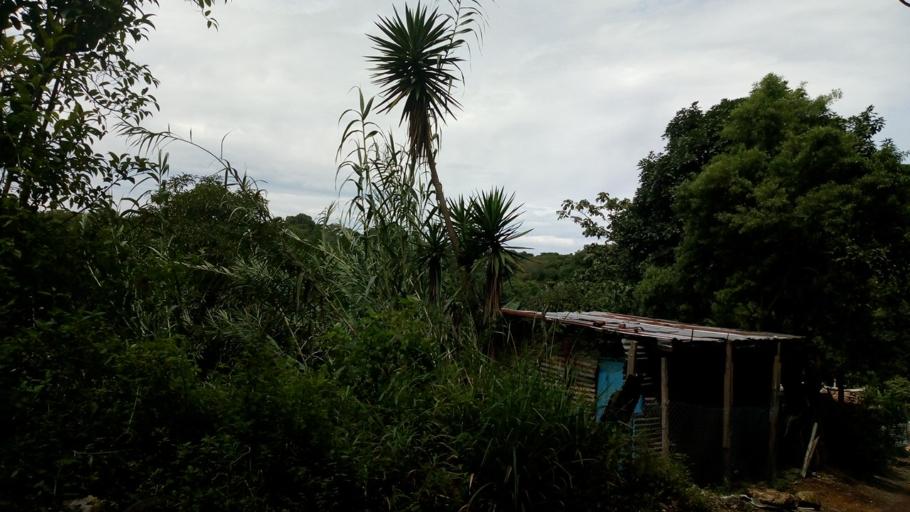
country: GT
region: Guatemala
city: Petapa
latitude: 14.5152
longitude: -90.5208
